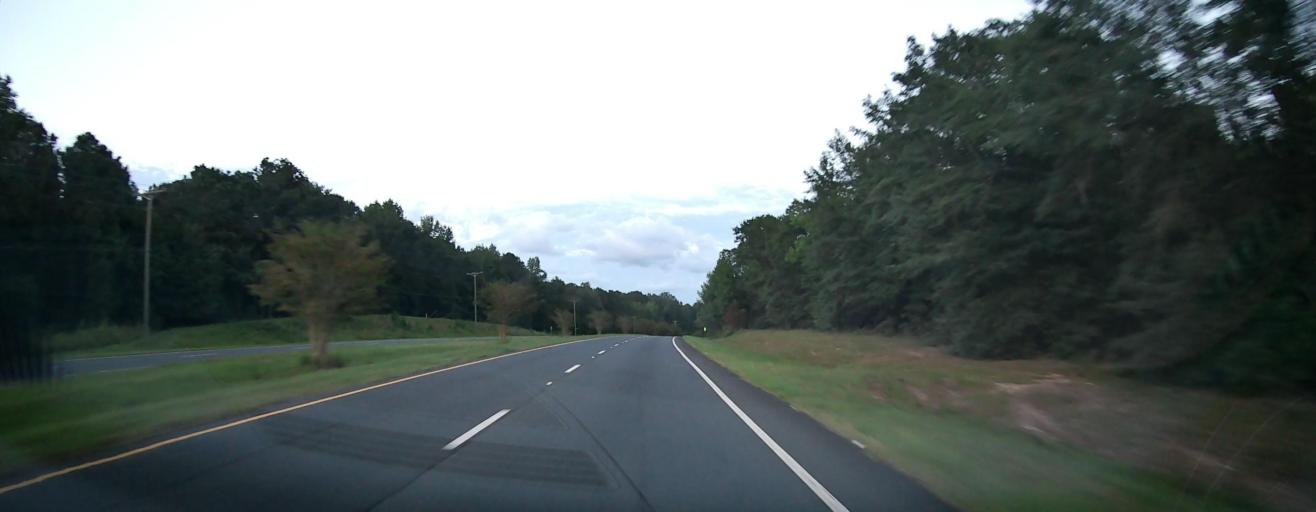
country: US
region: Georgia
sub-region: Harris County
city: Hamilton
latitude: 32.5548
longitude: -84.7579
